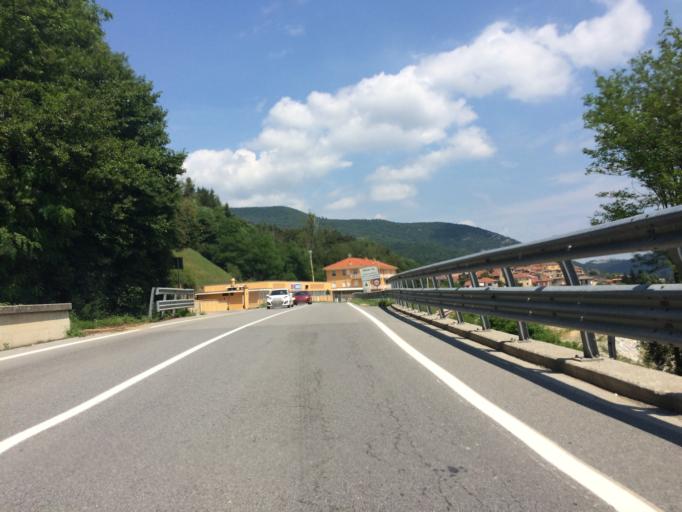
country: IT
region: Piedmont
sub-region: Provincia di Cuneo
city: Priola
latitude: 44.2546
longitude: 8.0201
